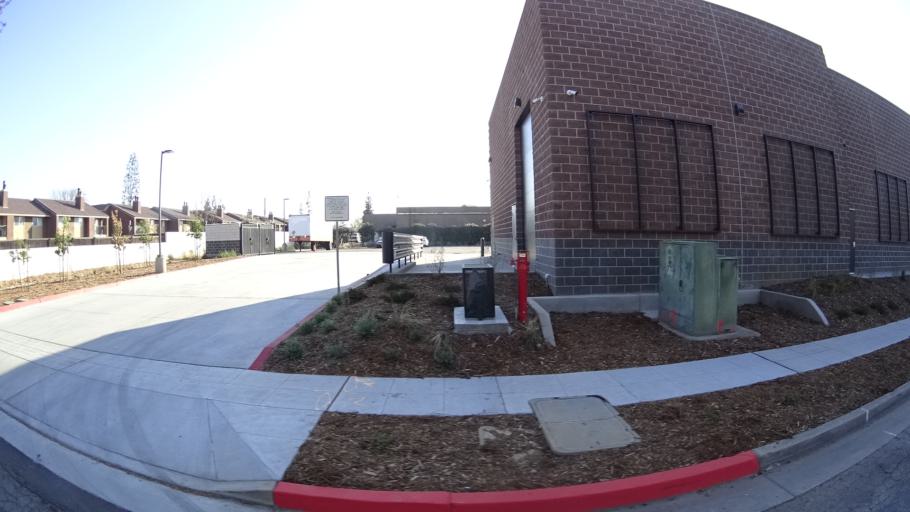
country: US
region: California
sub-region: Fresno County
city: Clovis
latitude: 36.8526
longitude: -119.7932
